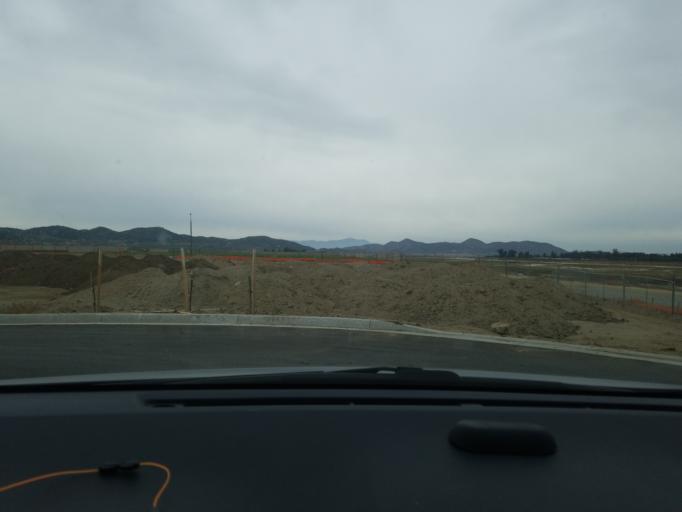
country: US
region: California
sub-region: Riverside County
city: Winchester
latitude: 33.6953
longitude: -117.1015
